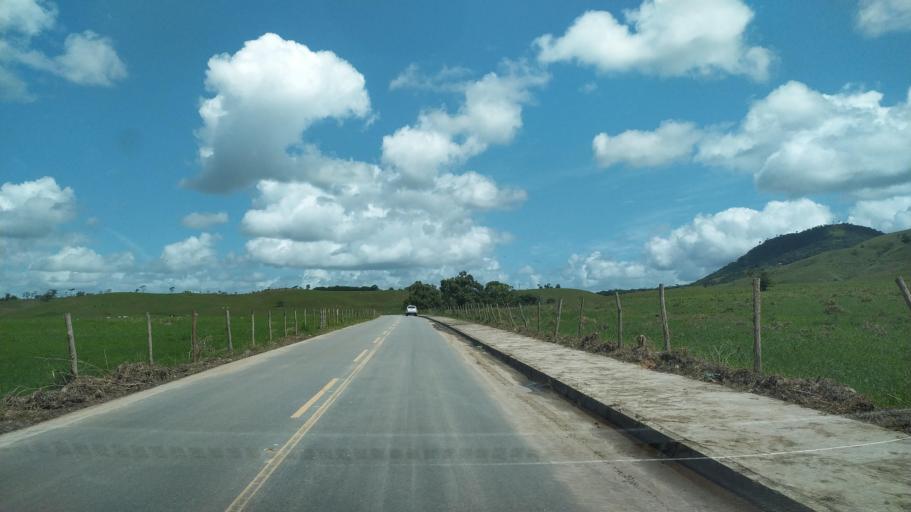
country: BR
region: Alagoas
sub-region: Uniao Dos Palmares
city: Uniao dos Palmares
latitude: -9.1594
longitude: -36.0453
